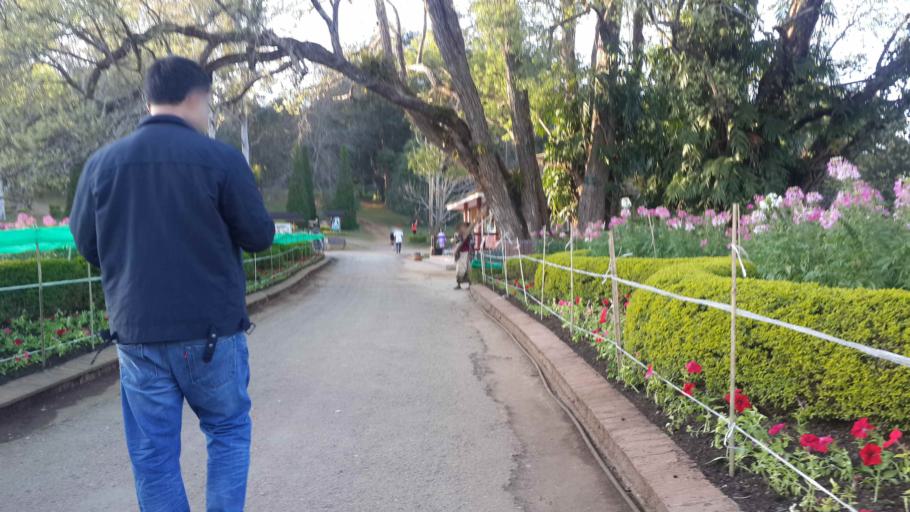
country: MM
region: Mandalay
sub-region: Pyin Oo Lwin District
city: Pyin Oo Lwin
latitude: 21.9936
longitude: 96.4698
